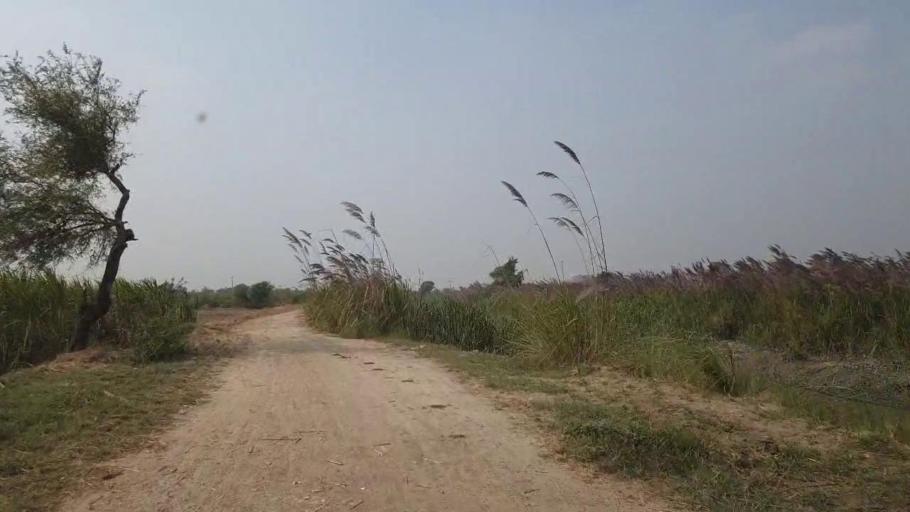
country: PK
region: Sindh
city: Matli
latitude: 25.0331
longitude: 68.5925
